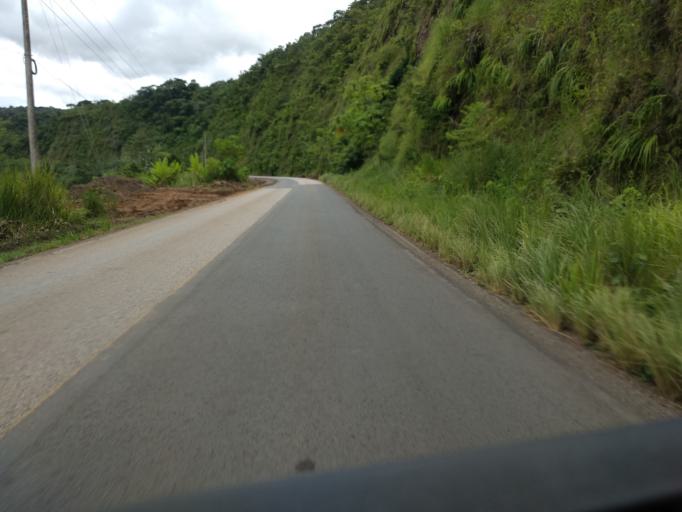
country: CR
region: Puntarenas
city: Buenos Aires
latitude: 9.0892
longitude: -83.2737
